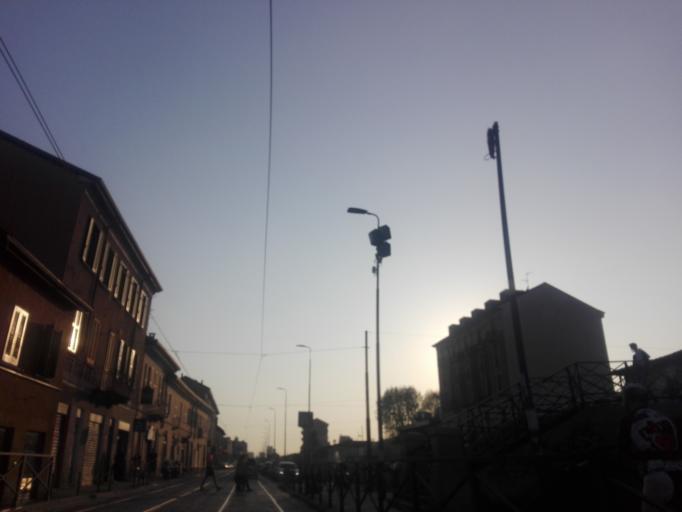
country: IT
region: Lombardy
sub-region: Citta metropolitana di Milano
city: Romano Banco
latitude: 45.4473
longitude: 9.1548
